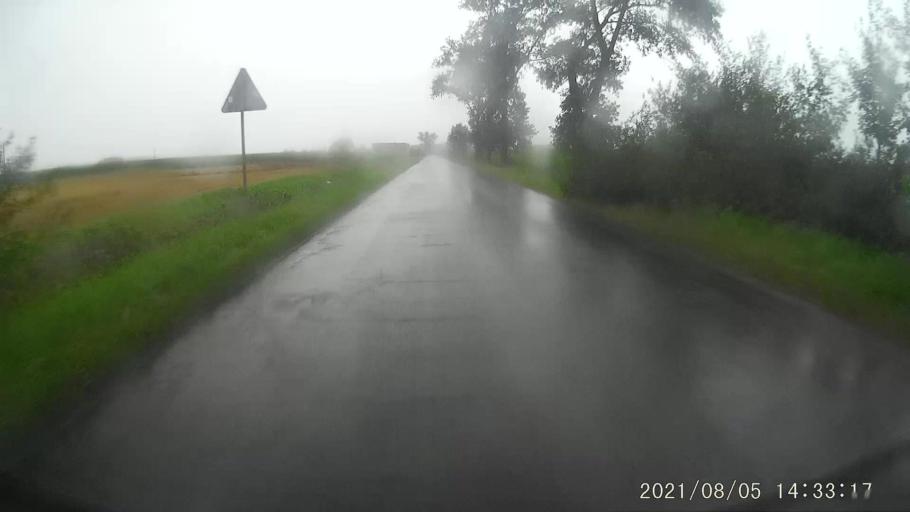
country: PL
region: Opole Voivodeship
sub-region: Powiat nyski
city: Korfantow
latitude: 50.4684
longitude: 17.5398
